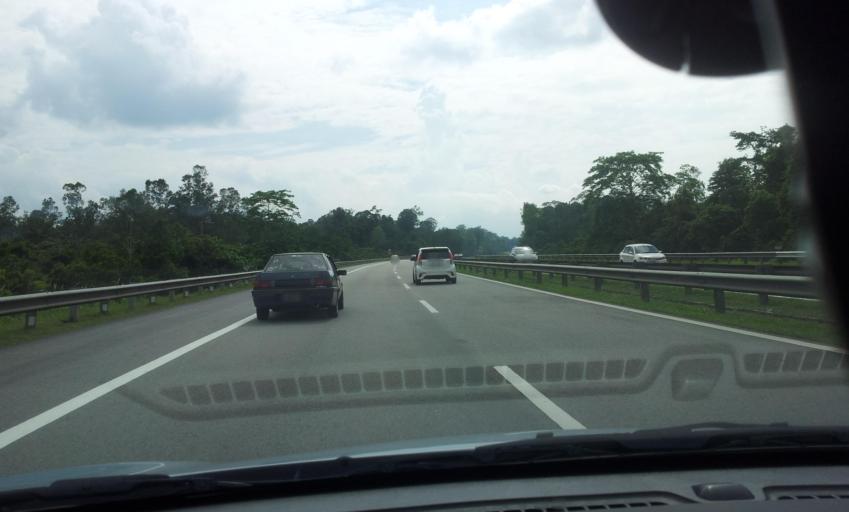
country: MY
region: Pahang
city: Kuantan
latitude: 3.7271
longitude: 102.9732
